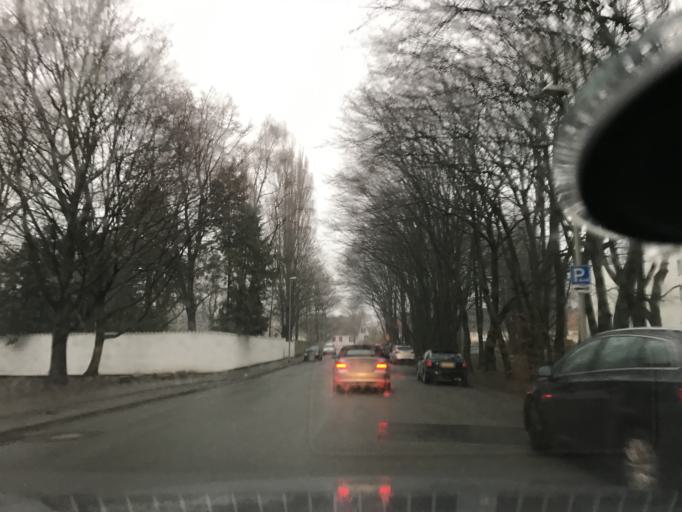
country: DE
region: Lower Saxony
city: Laatzen
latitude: 52.3530
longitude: 9.8253
